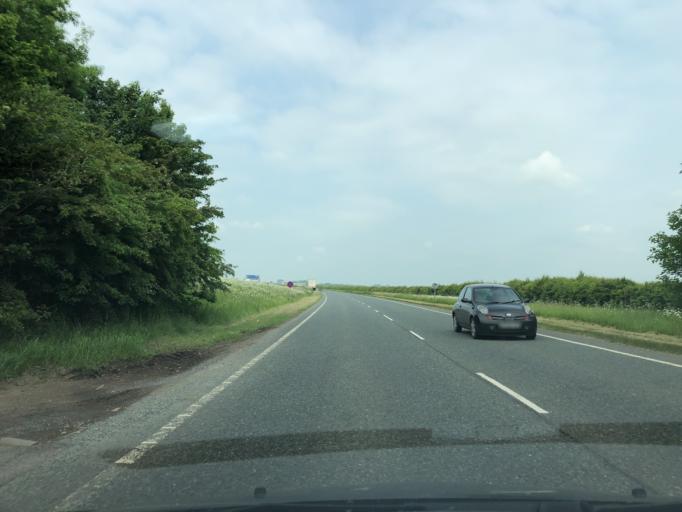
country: GB
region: England
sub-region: North Yorkshire
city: Boroughbridge
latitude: 54.1289
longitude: -1.4159
